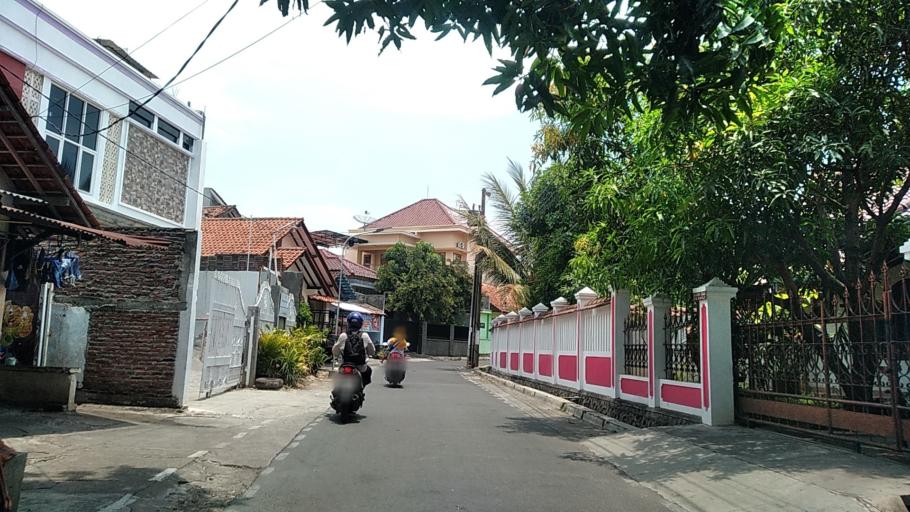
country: ID
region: Central Java
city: Semarang
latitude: -7.0621
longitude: 110.4114
